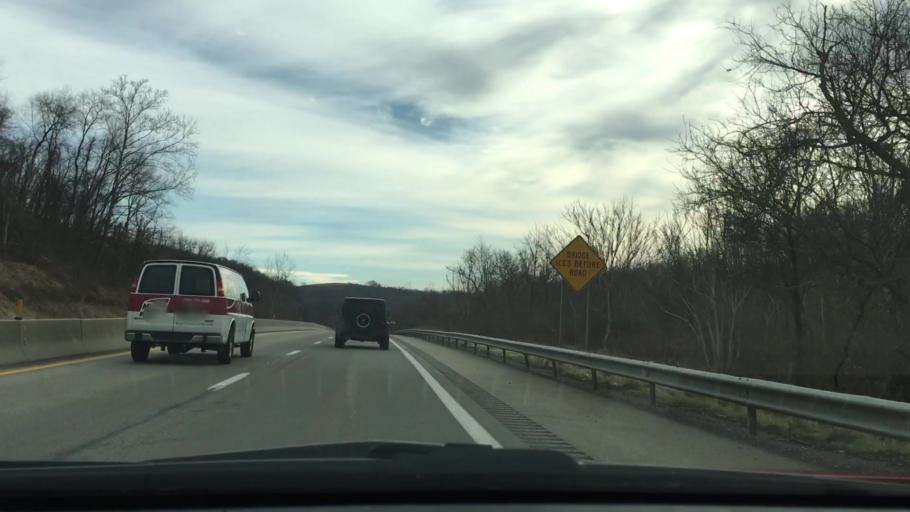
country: US
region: Pennsylvania
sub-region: Fayette County
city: Oliver
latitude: 39.9759
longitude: -79.7609
